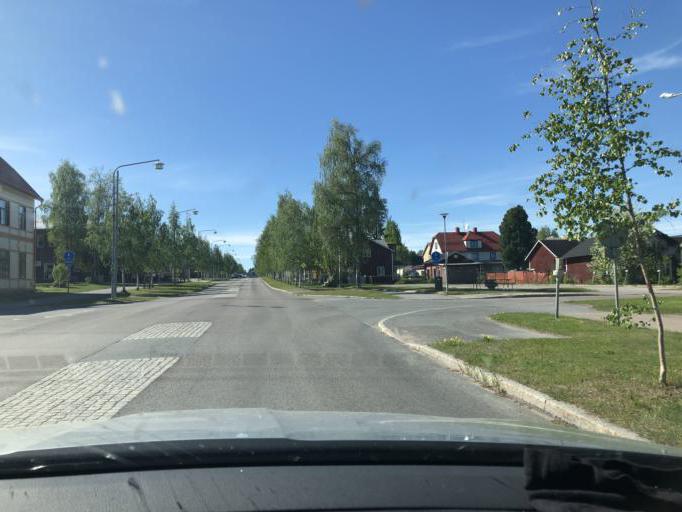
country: SE
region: Norrbotten
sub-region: Jokkmokks Kommun
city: Jokkmokk
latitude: 66.6054
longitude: 19.8343
